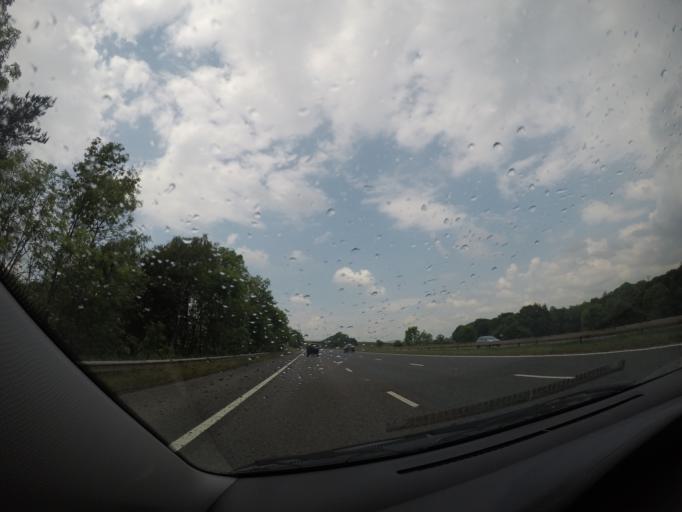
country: GB
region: England
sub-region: Cumbria
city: Penrith
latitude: 54.7442
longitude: -2.8112
